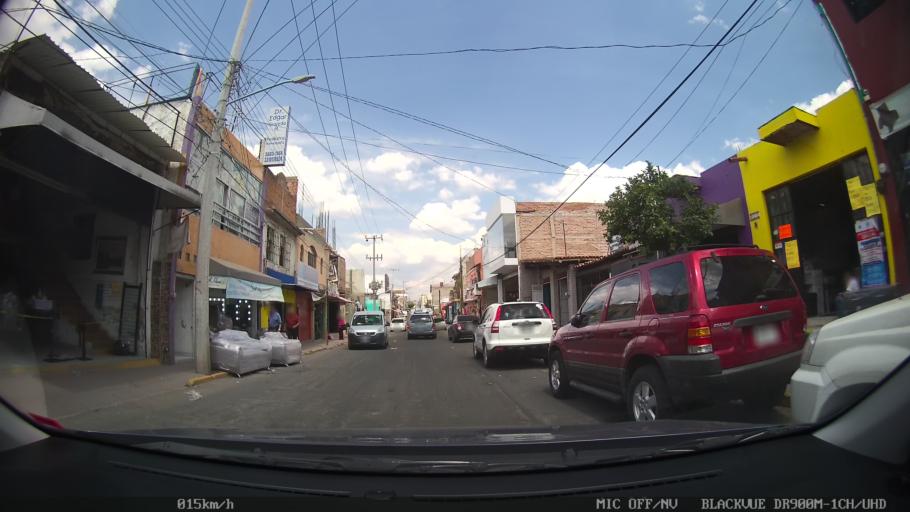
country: MX
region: Jalisco
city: Tonala
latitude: 20.6253
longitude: -103.2479
